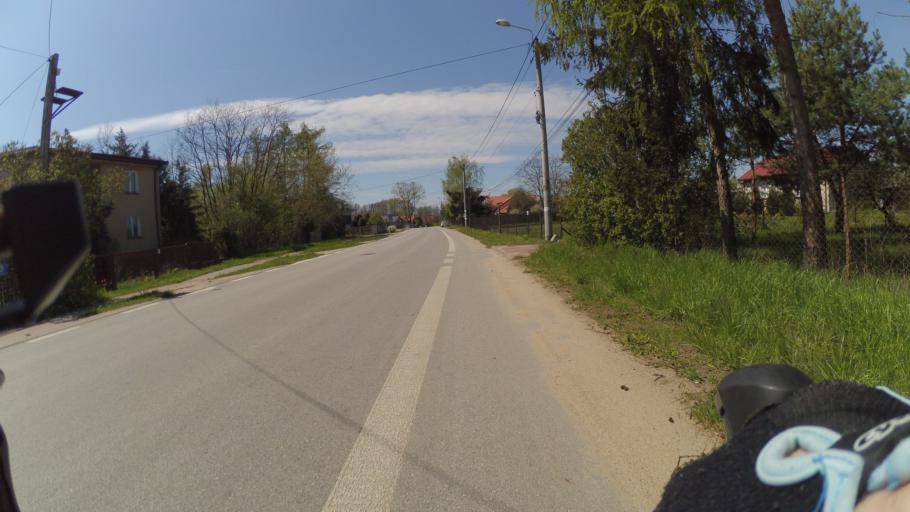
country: PL
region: Masovian Voivodeship
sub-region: Powiat nowodworski
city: Nowy Dwor Mazowiecki
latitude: 52.3913
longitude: 20.7082
